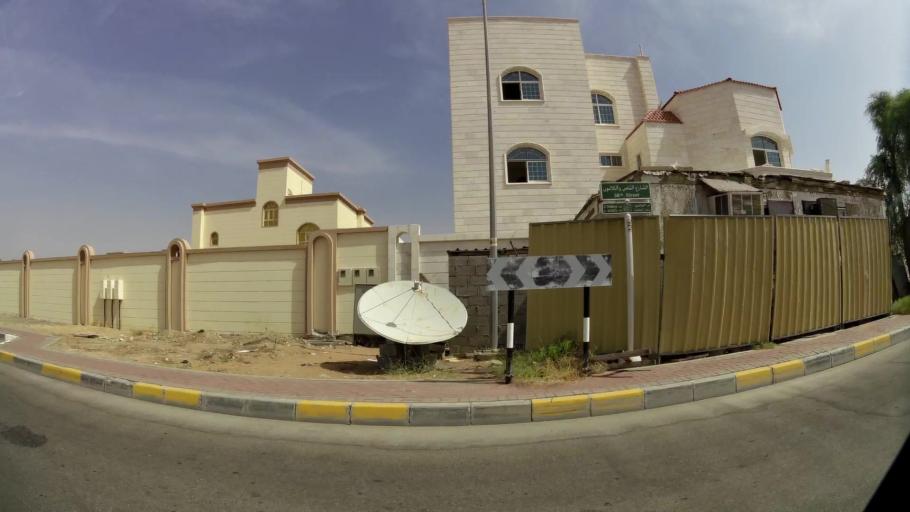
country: AE
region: Abu Dhabi
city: Al Ain
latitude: 24.1591
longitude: 55.6766
